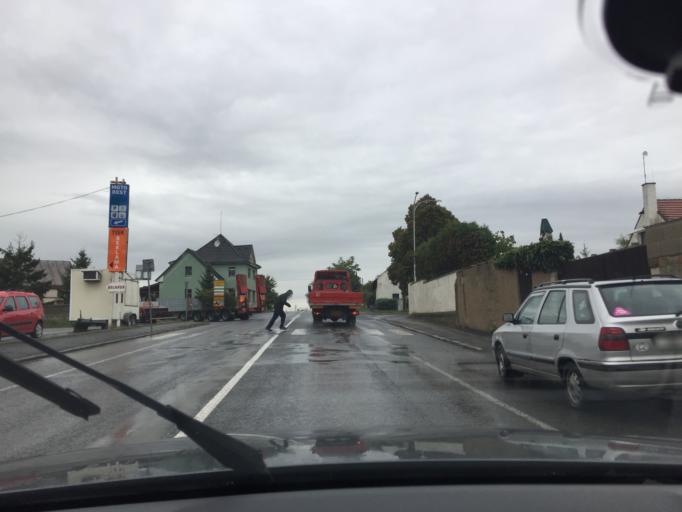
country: CZ
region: Central Bohemia
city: Klecany
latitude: 50.2023
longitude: 14.4342
